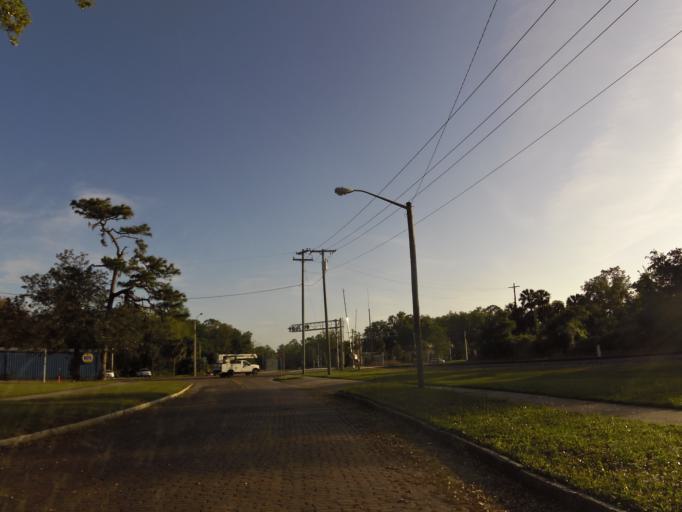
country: US
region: Florida
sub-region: Clay County
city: Green Cove Springs
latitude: 29.9910
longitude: -81.6852
